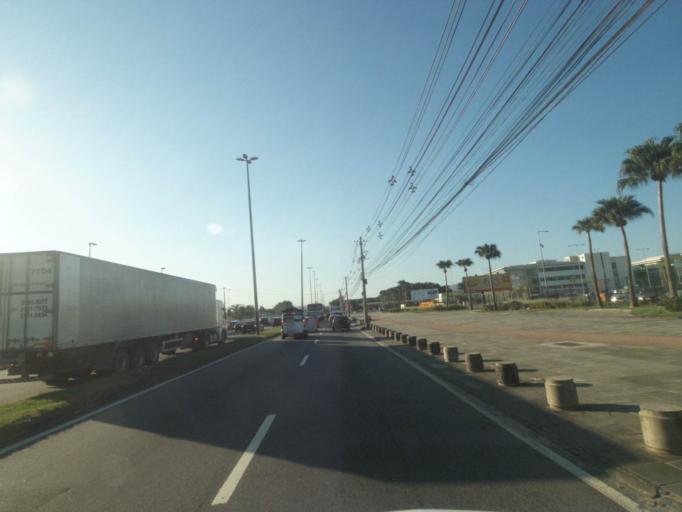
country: BR
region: Rio de Janeiro
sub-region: Rio De Janeiro
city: Rio de Janeiro
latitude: -22.9654
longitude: -43.3570
